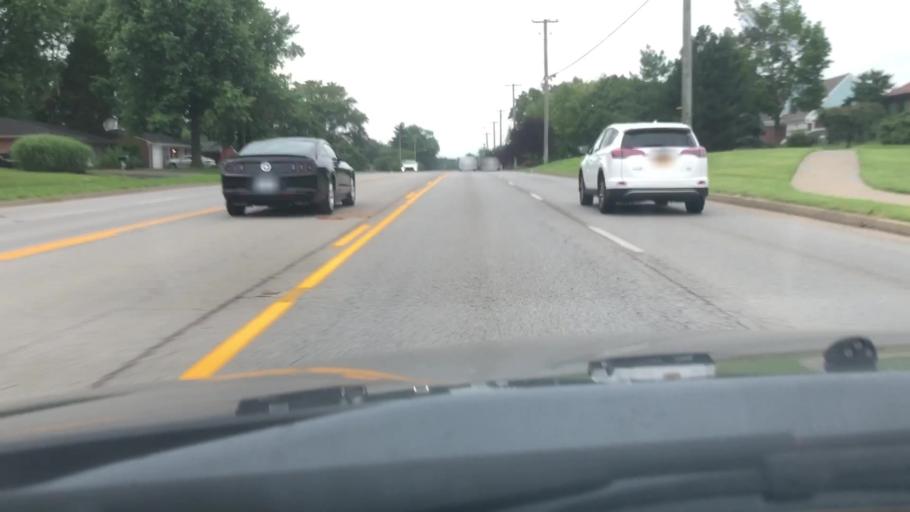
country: US
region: Kentucky
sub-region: Jefferson County
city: Barbourmeade
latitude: 38.2842
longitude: -85.5822
